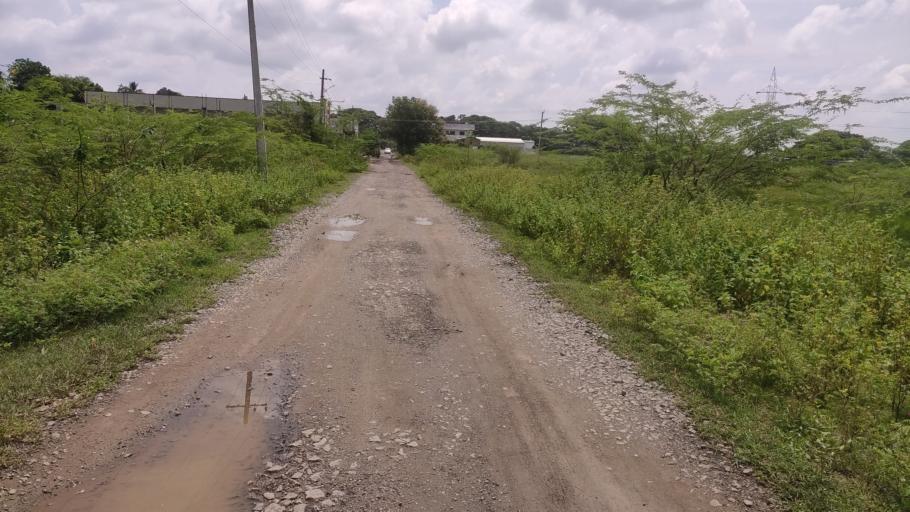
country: IN
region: Telangana
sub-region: Khammam
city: Khammam
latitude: 17.2444
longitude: 80.1936
